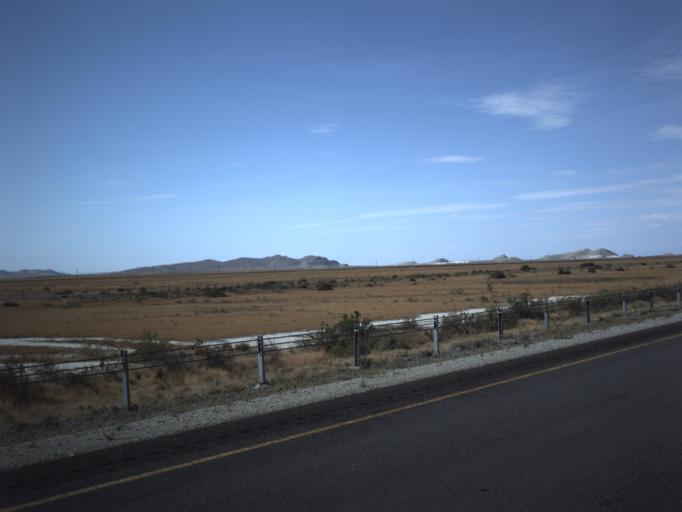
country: US
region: Utah
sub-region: Tooele County
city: Grantsville
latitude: 40.7268
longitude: -113.2104
